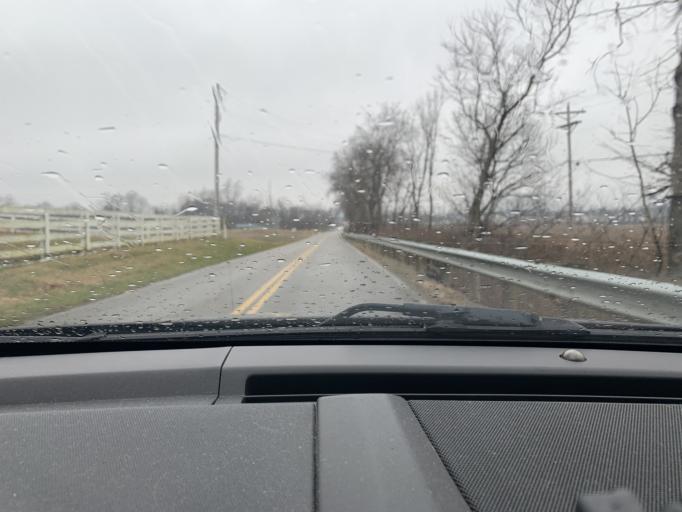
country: US
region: Ohio
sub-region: Ross County
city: Chillicothe
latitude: 39.3851
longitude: -82.9579
